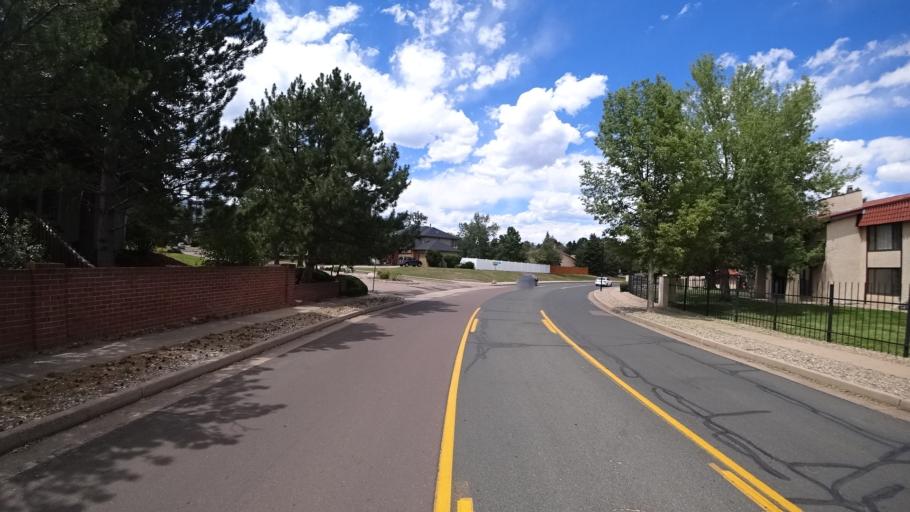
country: US
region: Colorado
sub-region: El Paso County
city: Stratmoor
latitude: 38.7872
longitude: -104.8246
